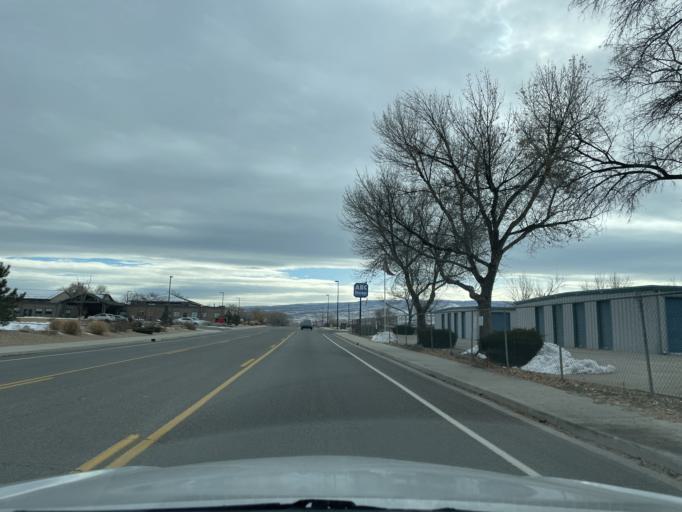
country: US
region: Colorado
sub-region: Mesa County
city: Grand Junction
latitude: 39.0866
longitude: -108.5802
